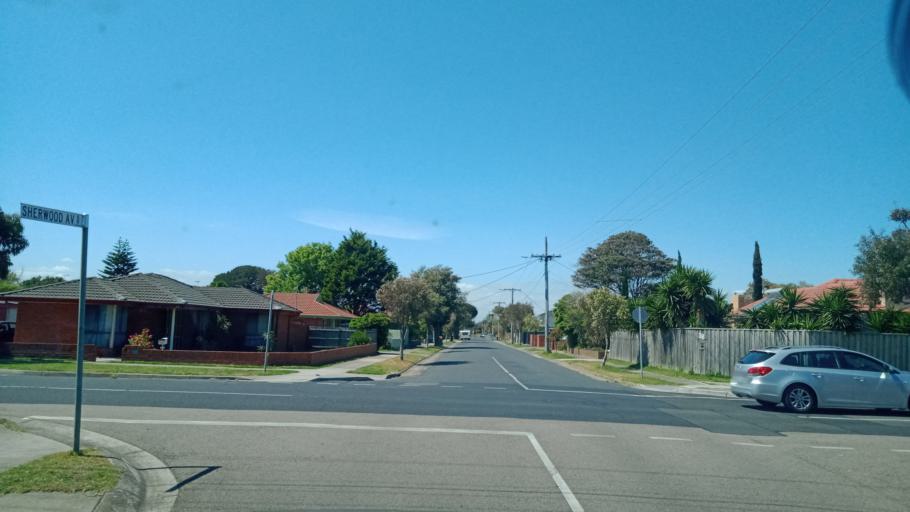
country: AU
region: Victoria
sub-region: Kingston
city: Chelsea
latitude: -38.0527
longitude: 145.1216
